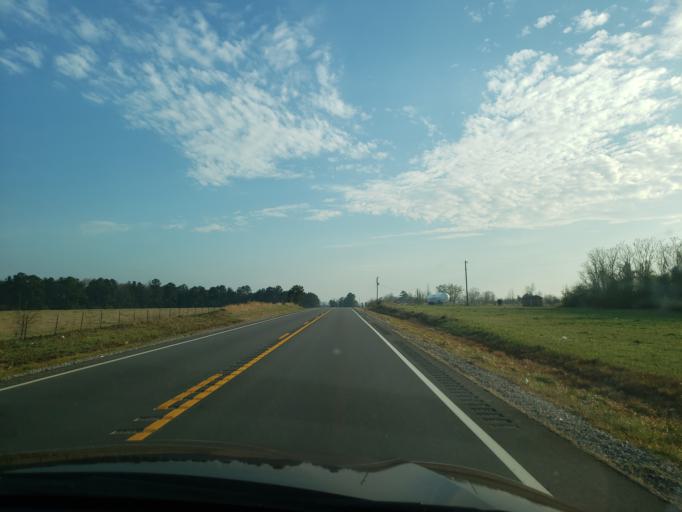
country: US
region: Alabama
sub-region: Hale County
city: Moundville
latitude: 32.8710
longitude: -87.6117
